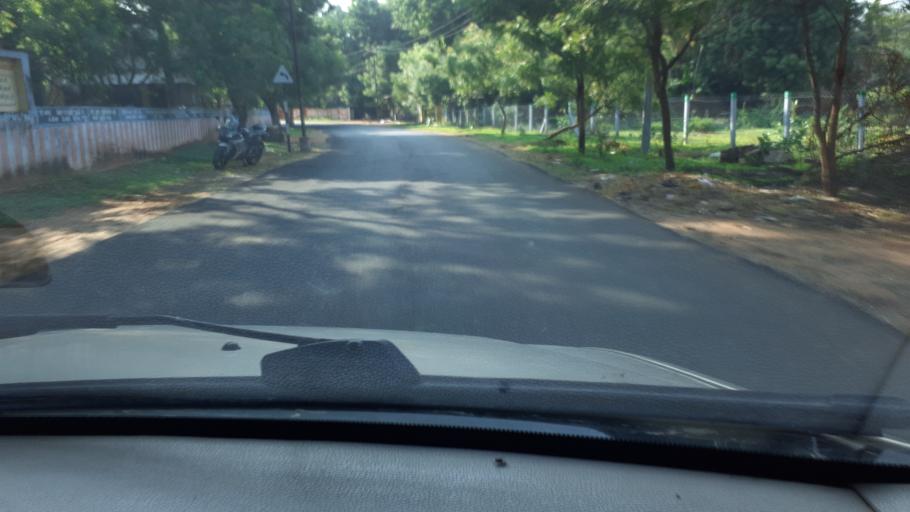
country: IN
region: Tamil Nadu
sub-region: Thoothukkudi
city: Eral
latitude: 8.5789
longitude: 78.0241
